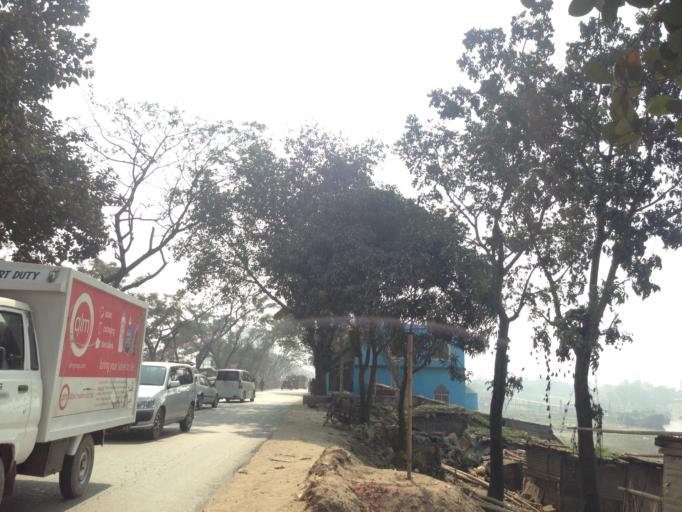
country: BD
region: Dhaka
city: Azimpur
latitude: 23.8030
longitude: 90.3438
